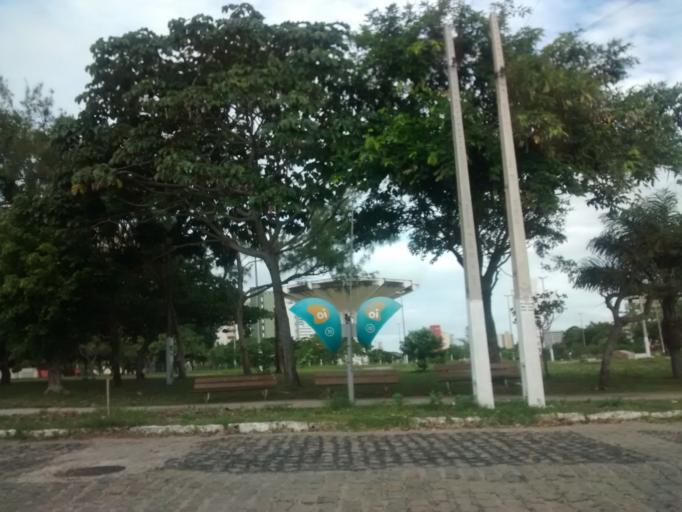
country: BR
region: Rio Grande do Norte
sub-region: Natal
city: Natal
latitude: -5.8743
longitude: -35.1820
